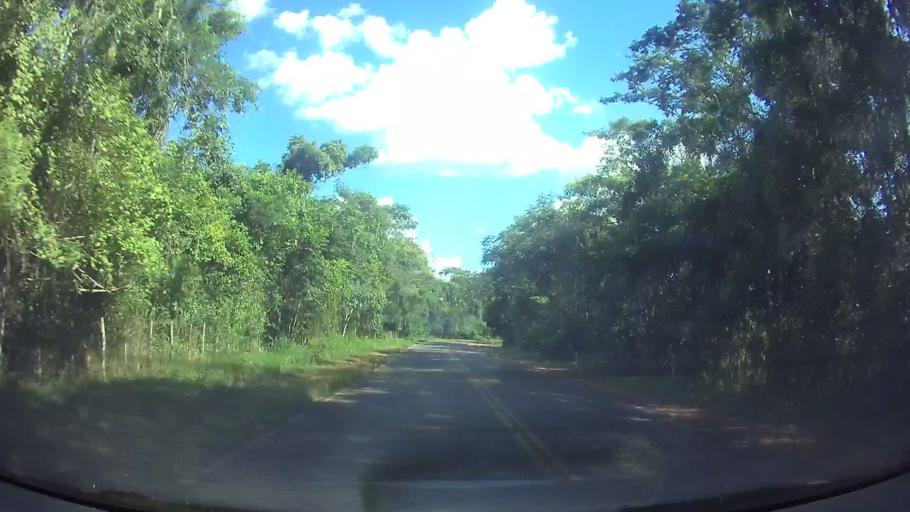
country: PY
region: Paraguari
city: Sapucai
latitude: -25.6659
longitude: -56.8577
